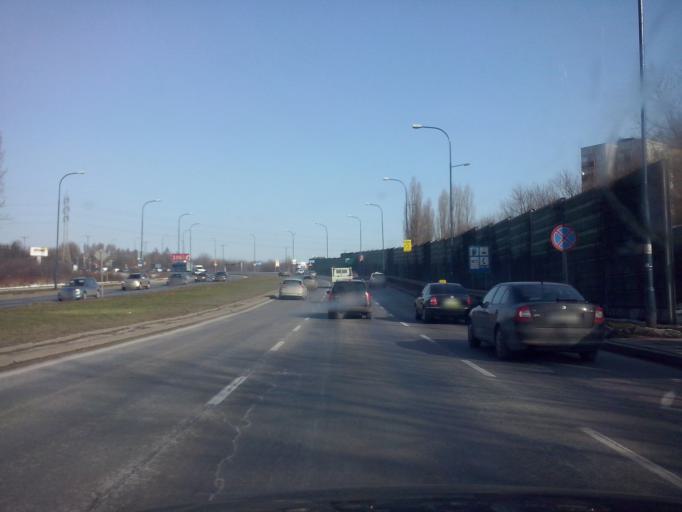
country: PL
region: Lesser Poland Voivodeship
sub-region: Krakow
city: Krakow
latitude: 50.0848
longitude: 20.0005
